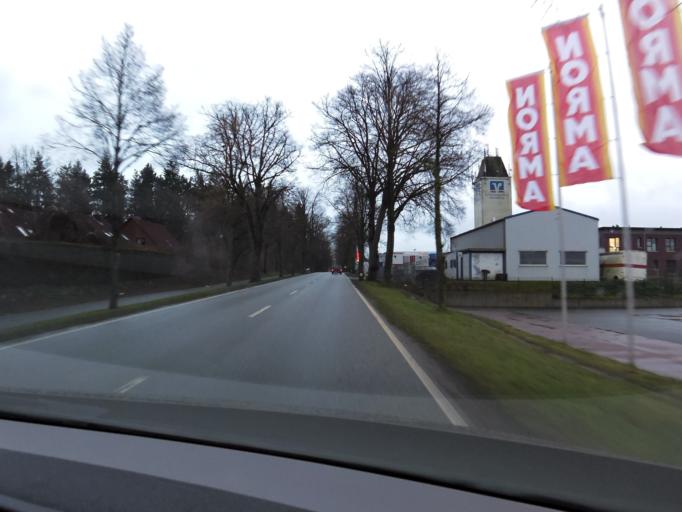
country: DE
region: Schleswig-Holstein
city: Ratzeburg
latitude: 53.6916
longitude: 10.7997
